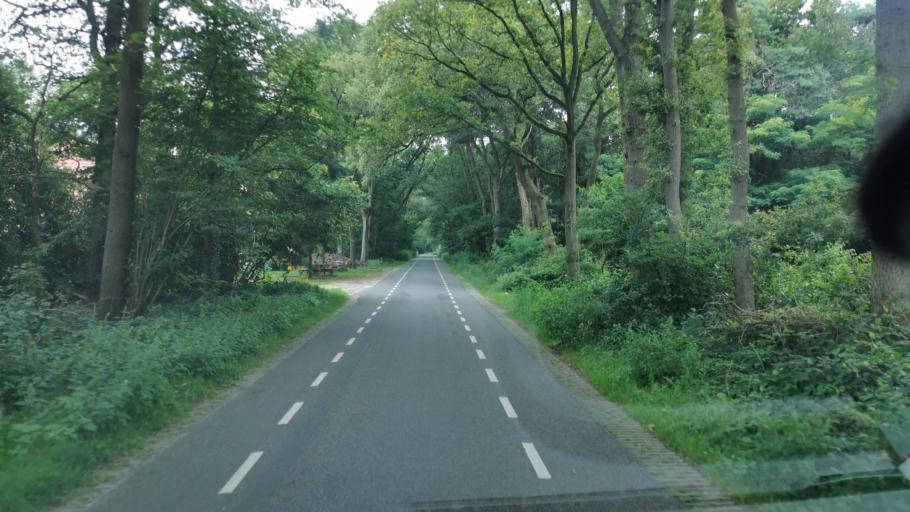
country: NL
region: Overijssel
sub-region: Gemeente Haaksbergen
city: Haaksbergen
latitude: 52.1506
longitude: 6.8134
